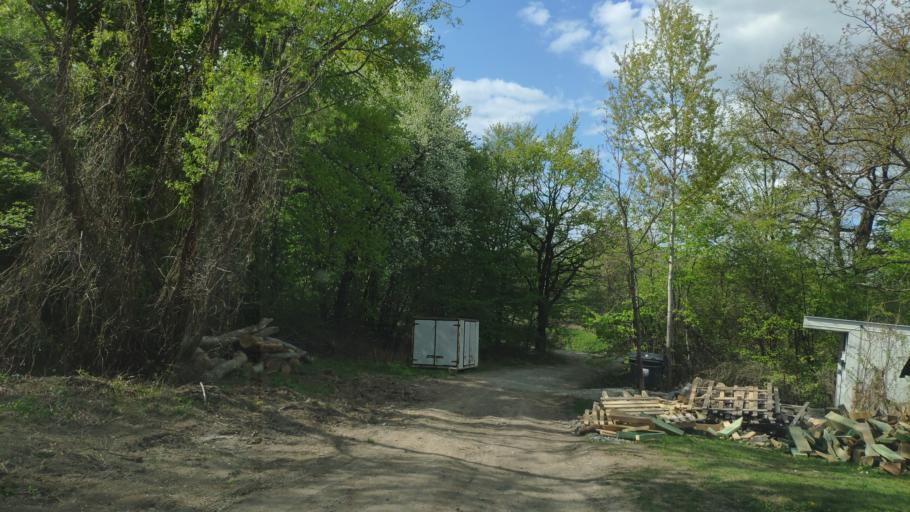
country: SK
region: Kosicky
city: Kosice
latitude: 48.6764
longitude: 21.4455
